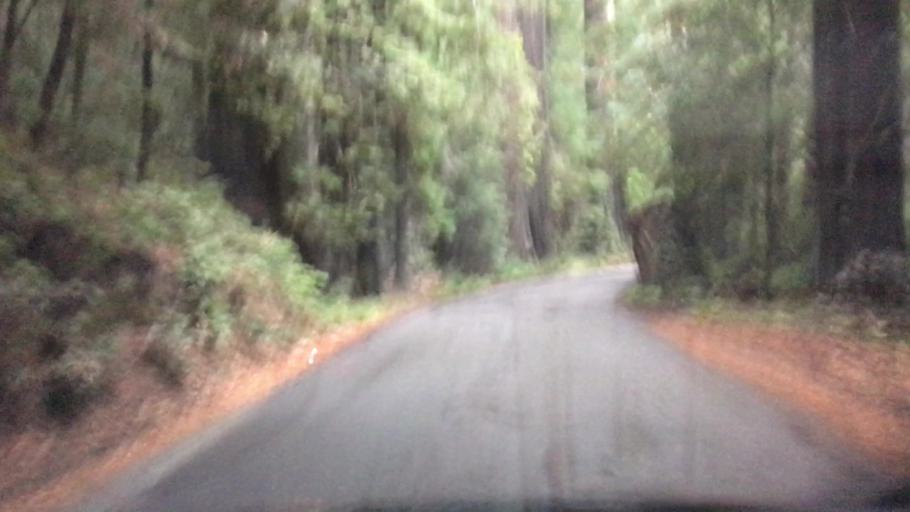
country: US
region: California
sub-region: Humboldt County
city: Rio Dell
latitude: 40.3523
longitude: -123.9818
